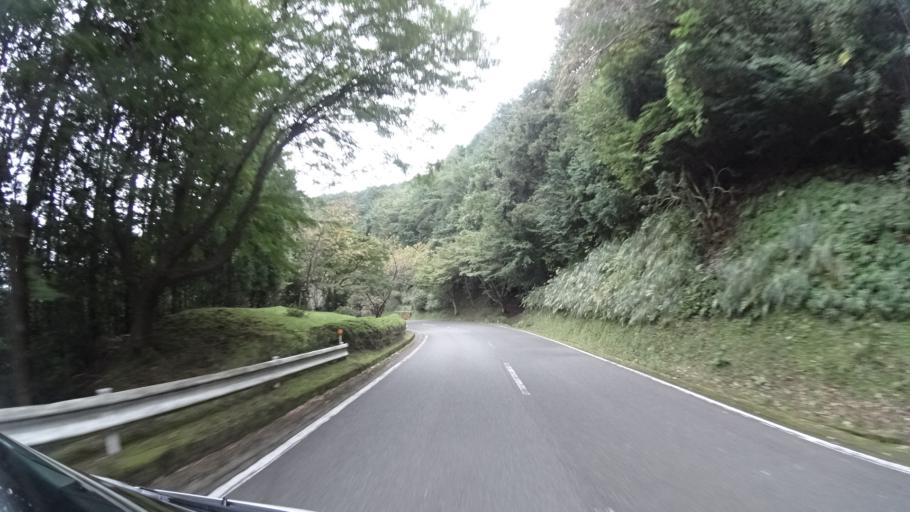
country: JP
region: Shiga Prefecture
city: Kitahama
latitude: 35.1046
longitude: 135.8544
